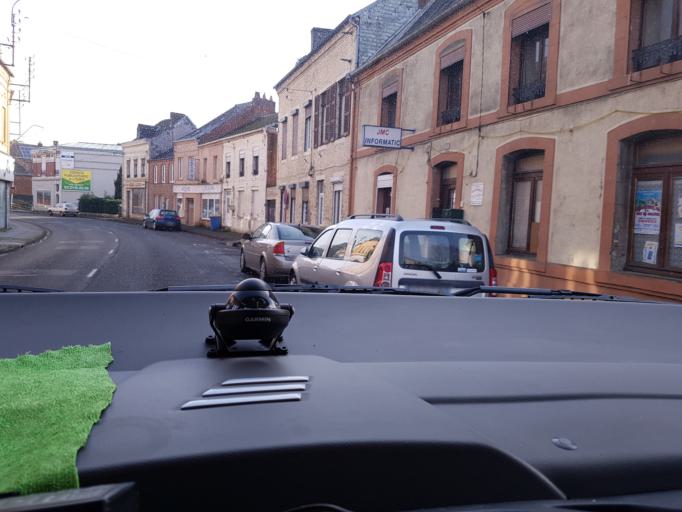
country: FR
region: Picardie
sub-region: Departement de l'Aisne
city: Hirson
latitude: 49.9250
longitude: 4.0772
